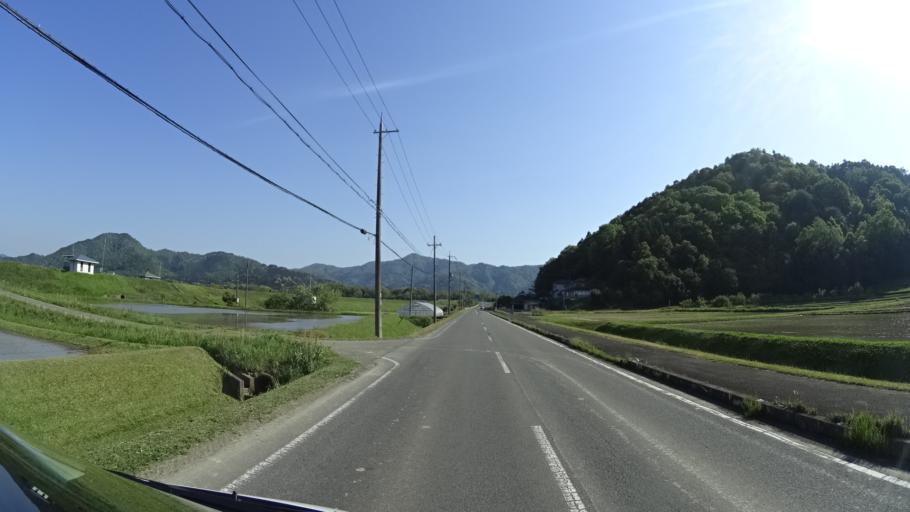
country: JP
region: Kyoto
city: Ayabe
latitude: 35.3144
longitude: 135.2089
